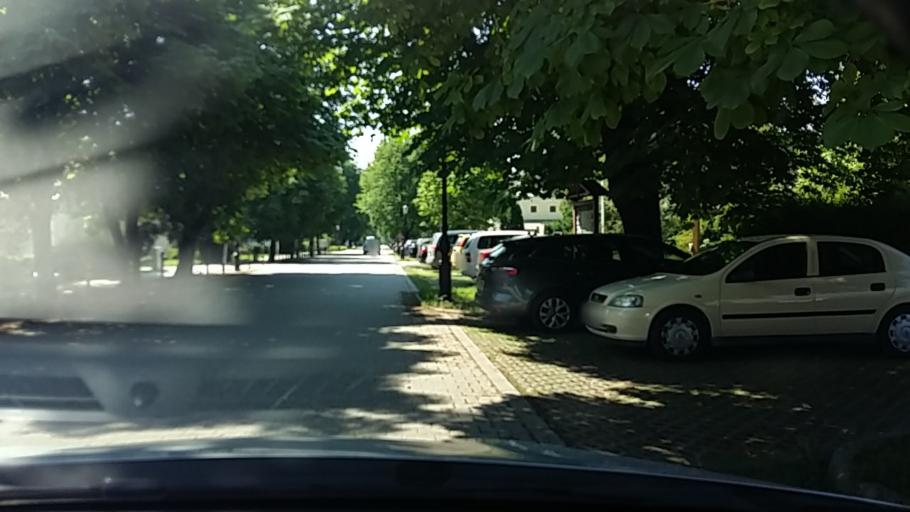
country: HU
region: Fejer
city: Etyek
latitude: 47.5021
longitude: 18.7519
